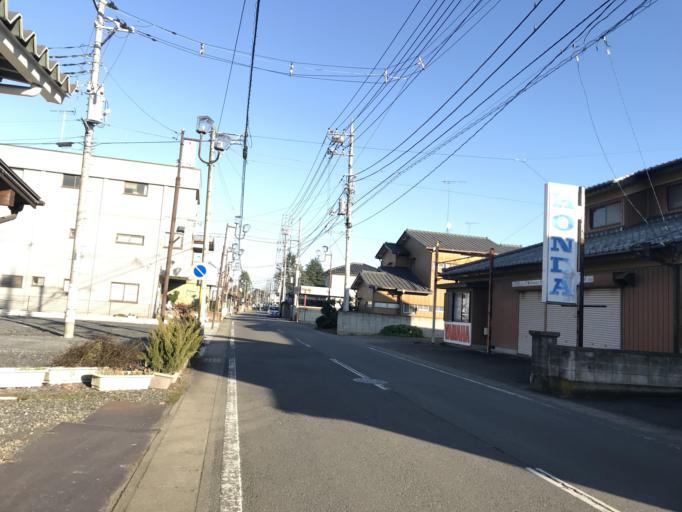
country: JP
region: Ibaraki
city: Yuki
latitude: 36.3031
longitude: 139.8795
